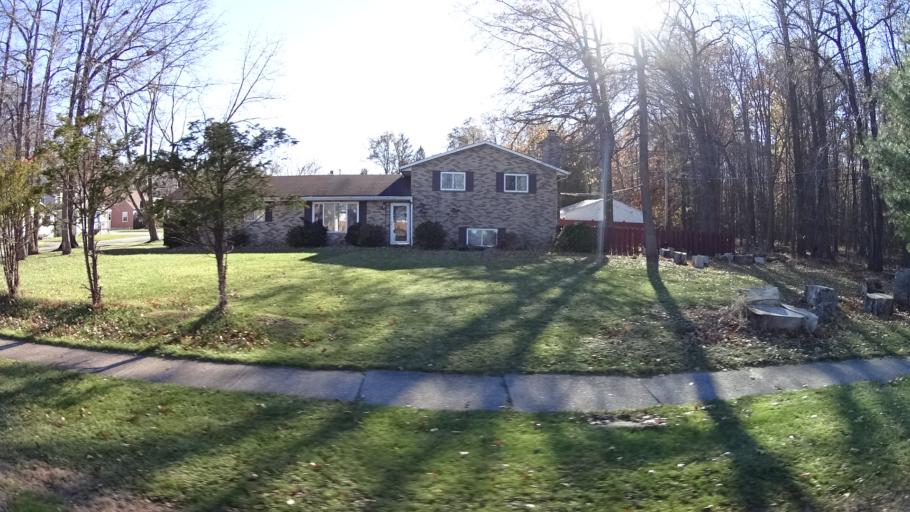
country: US
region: Ohio
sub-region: Lorain County
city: Avon Lake
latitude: 41.5107
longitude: -82.0050
